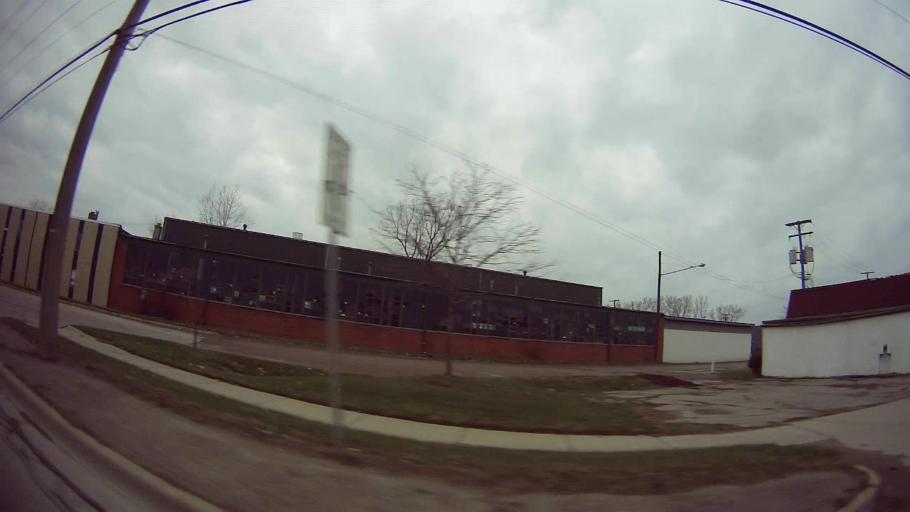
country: US
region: Michigan
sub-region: Macomb County
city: Warren
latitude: 42.4498
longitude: -83.0022
